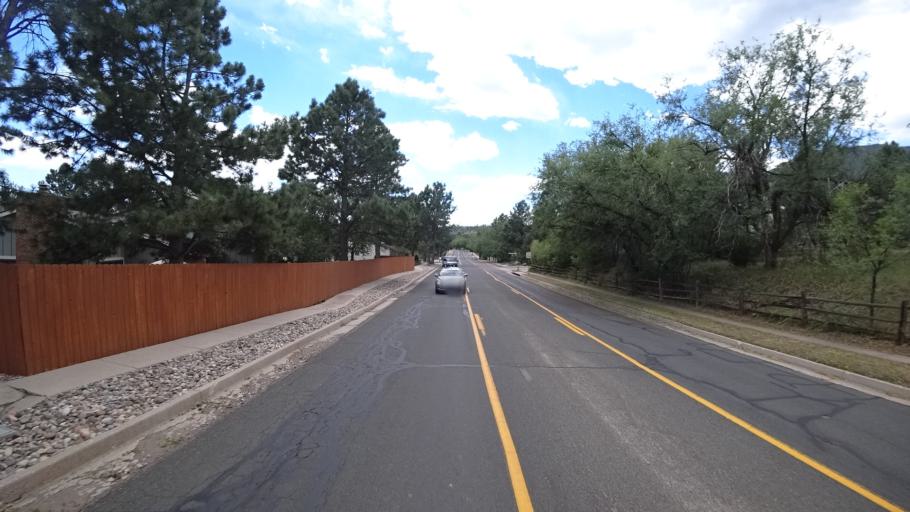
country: US
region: Colorado
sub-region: El Paso County
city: Stratmoor
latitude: 38.7811
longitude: -104.8315
